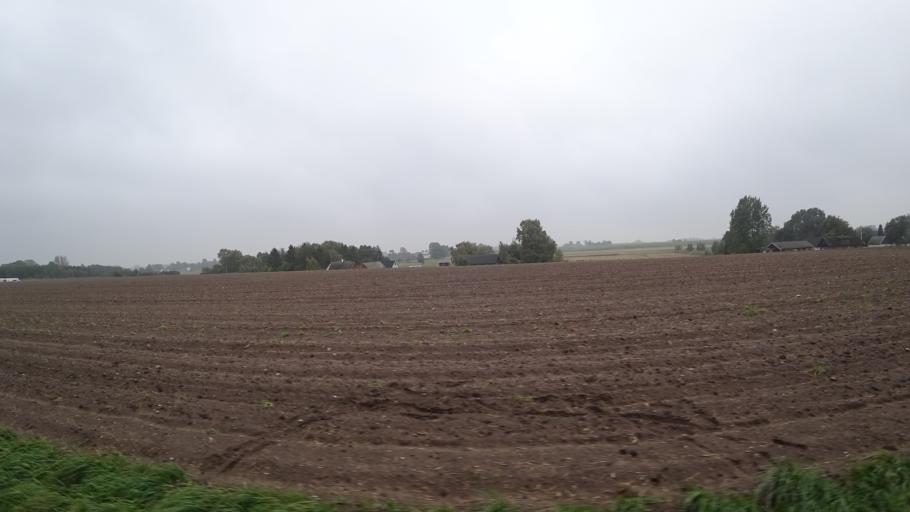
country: SE
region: Skane
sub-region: Kavlinge Kommun
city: Kaevlinge
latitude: 55.8152
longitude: 13.0839
